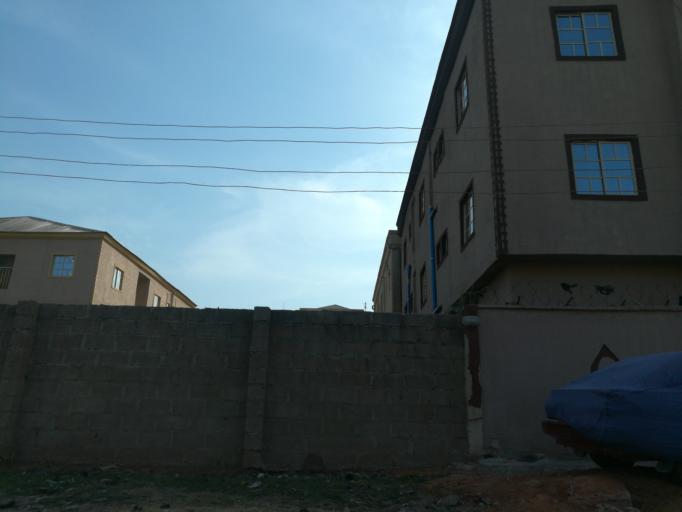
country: NG
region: Kano
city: Kano
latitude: 12.0273
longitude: 8.5265
